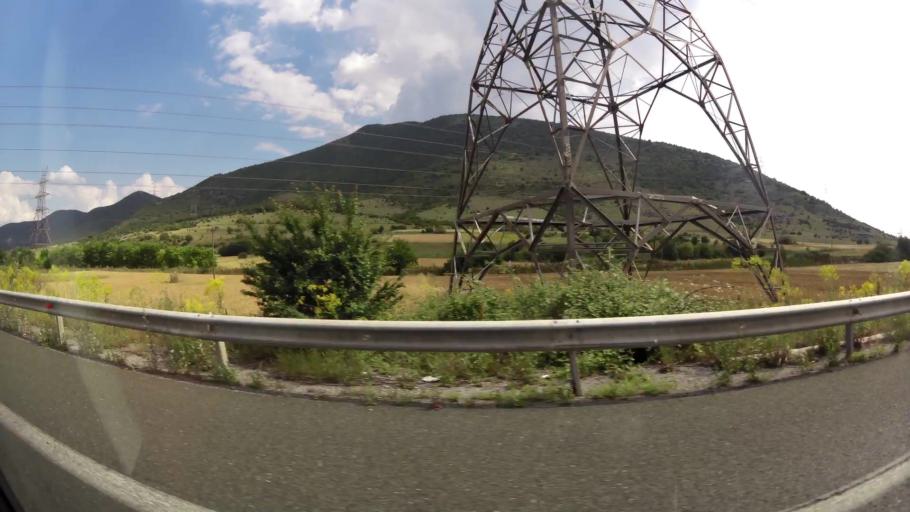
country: GR
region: West Macedonia
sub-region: Nomos Kozanis
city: Akrini
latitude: 40.3691
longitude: 21.8951
